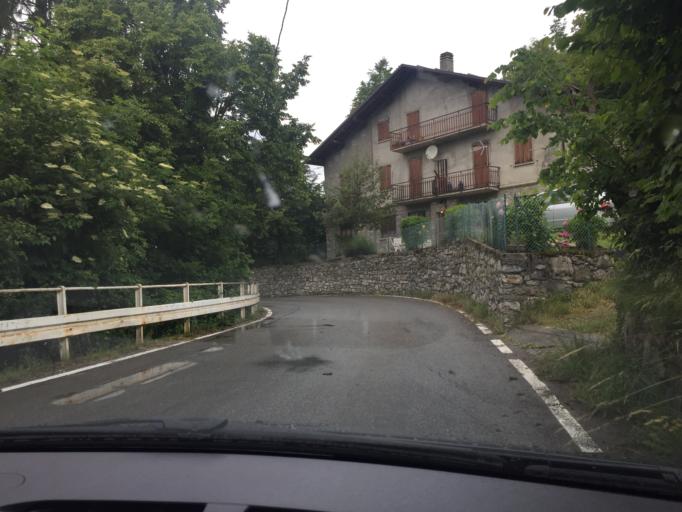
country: IT
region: Lombardy
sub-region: Provincia di Lecco
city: Esino Lario
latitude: 45.9972
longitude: 9.3422
